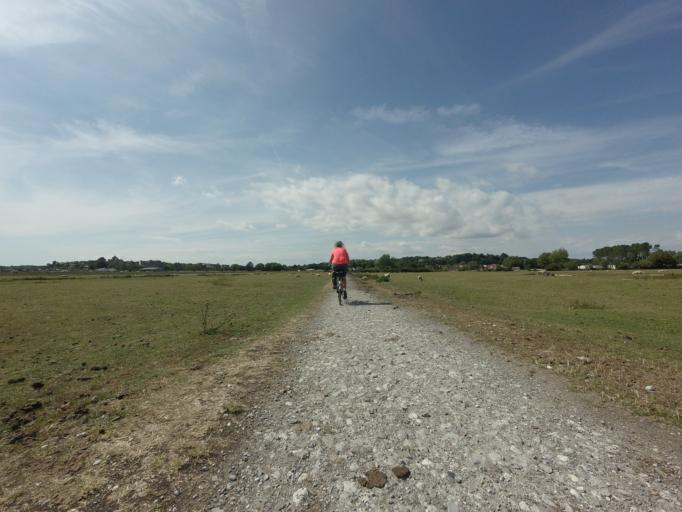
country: GB
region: England
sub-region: East Sussex
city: Rye
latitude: 50.9507
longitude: 0.7463
